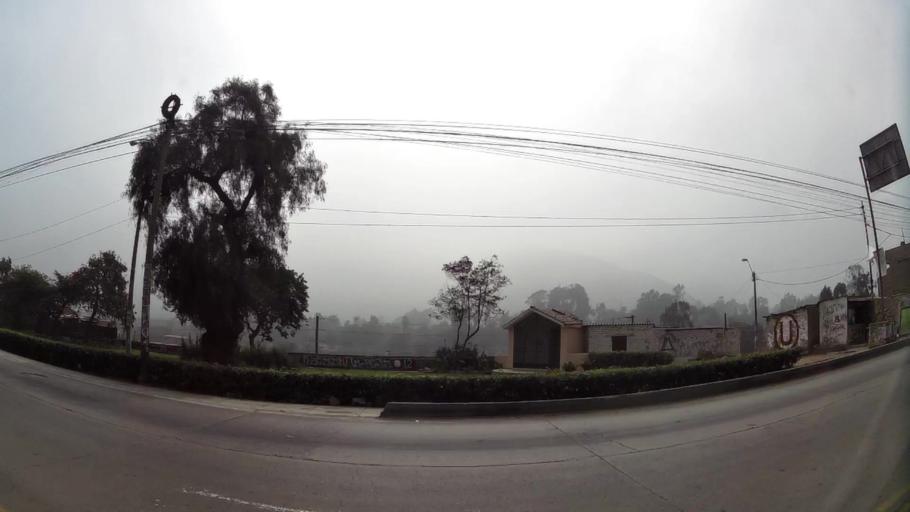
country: PE
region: Lima
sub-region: Lima
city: Chaclacayo
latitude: -11.9686
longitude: -76.7470
